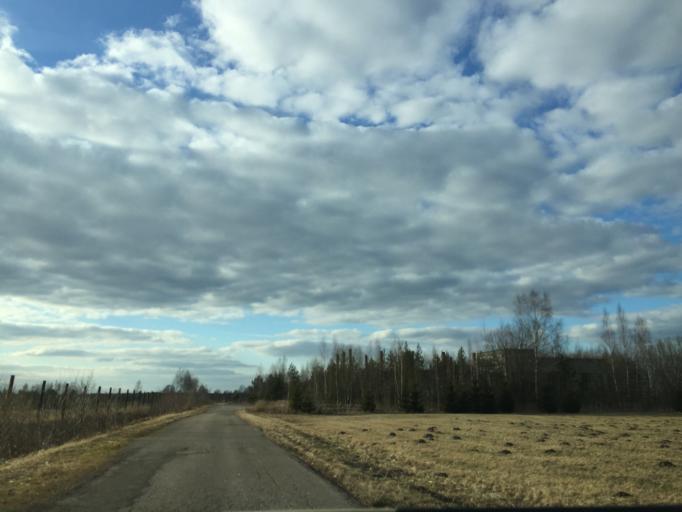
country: LV
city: Tireli
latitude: 56.8712
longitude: 23.6161
